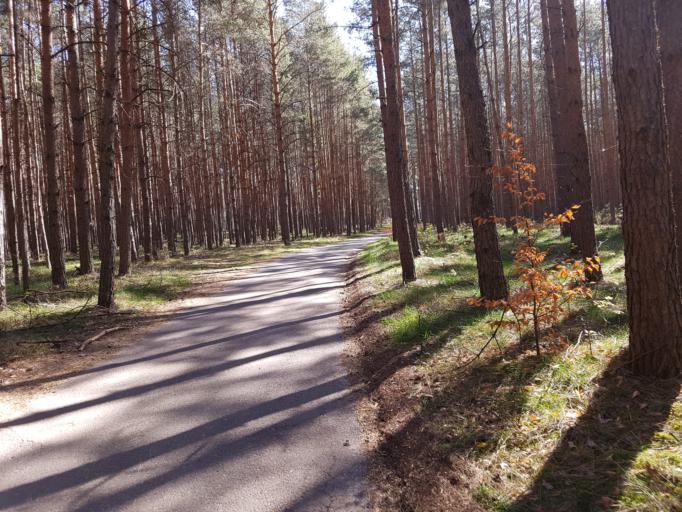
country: DE
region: Brandenburg
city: Groden
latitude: 51.3868
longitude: 13.5623
